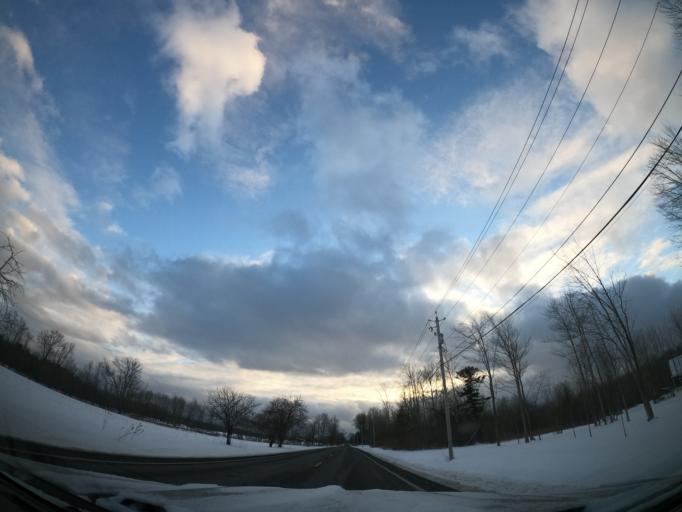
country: US
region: New York
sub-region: Onondaga County
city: Brewerton
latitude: 43.2125
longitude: -76.1564
